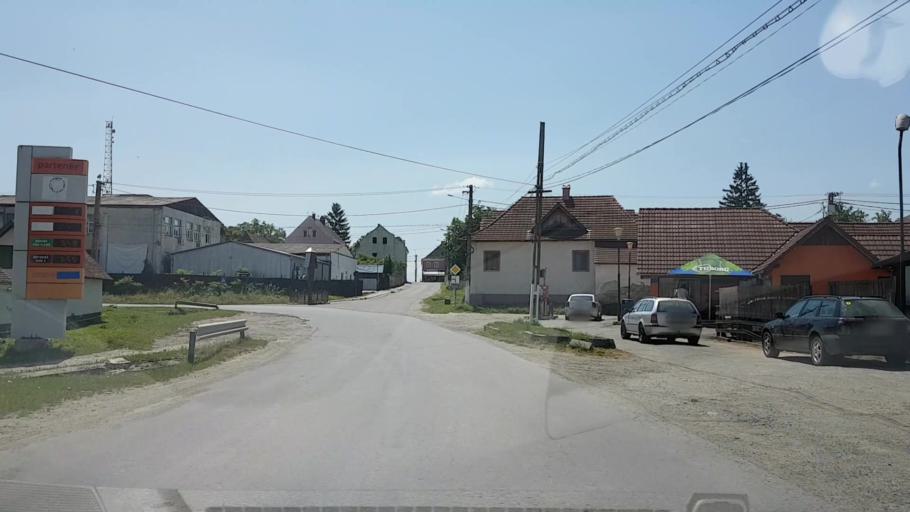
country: RO
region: Brasov
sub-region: Comuna Cincu
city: Cincu
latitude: 45.9170
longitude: 24.8015
